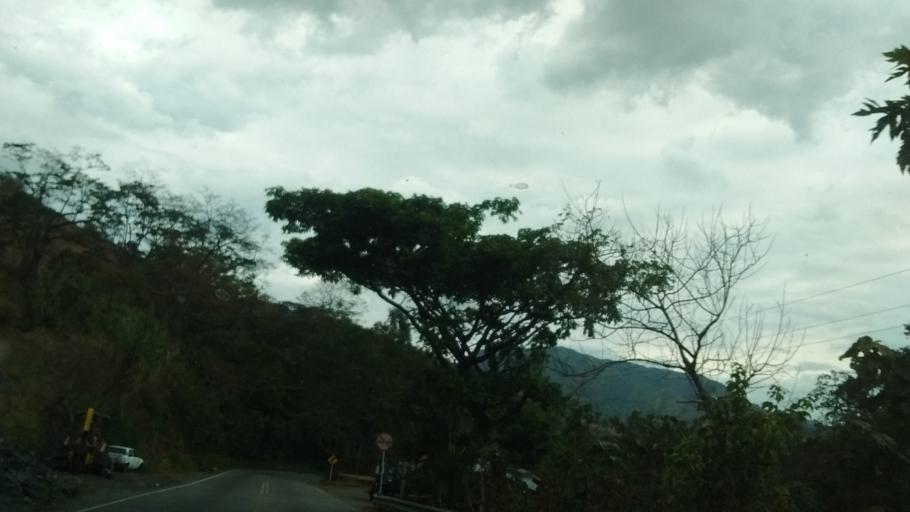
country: CO
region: Cauca
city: Rosas
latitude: 2.2829
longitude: -76.7016
